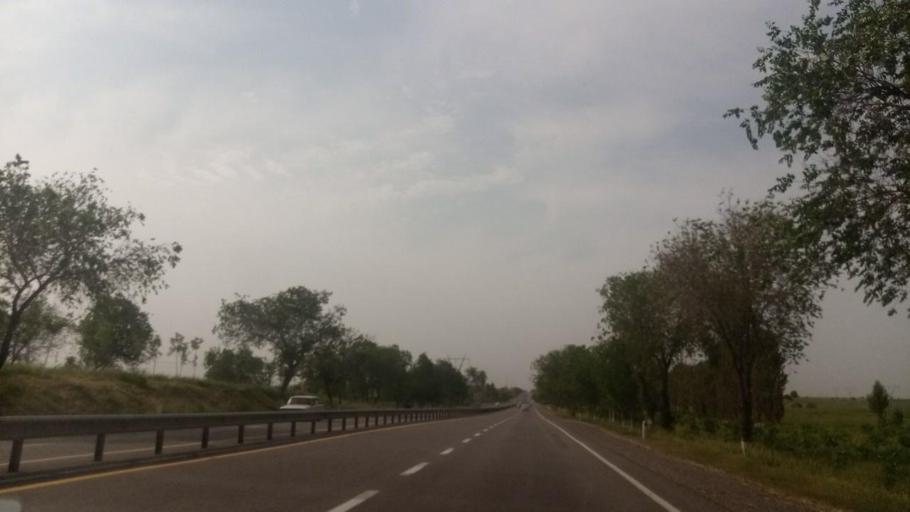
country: UZ
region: Toshkent
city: Tuytepa
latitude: 41.0693
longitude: 69.4781
